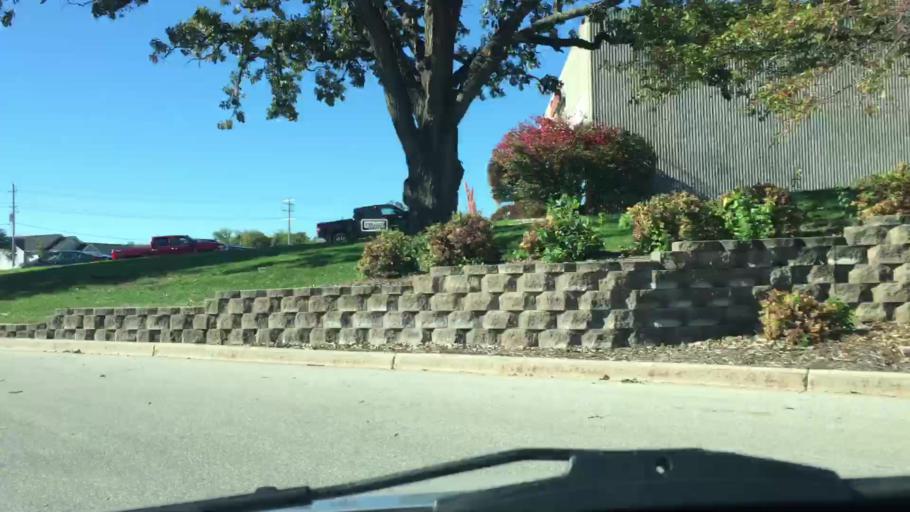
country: US
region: Wisconsin
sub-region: Waukesha County
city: Waukesha
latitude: 43.0372
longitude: -88.1816
